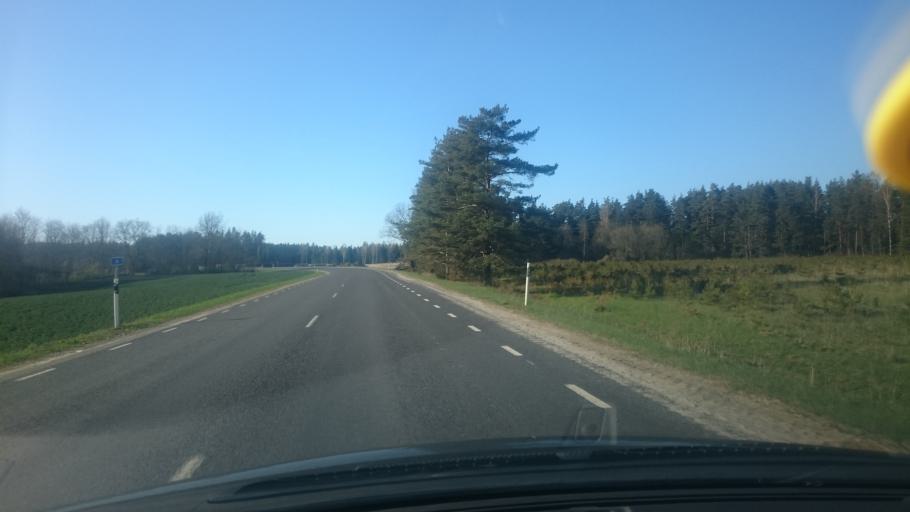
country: EE
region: Harju
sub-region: Raasiku vald
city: Raasiku
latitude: 59.1552
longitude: 25.1920
